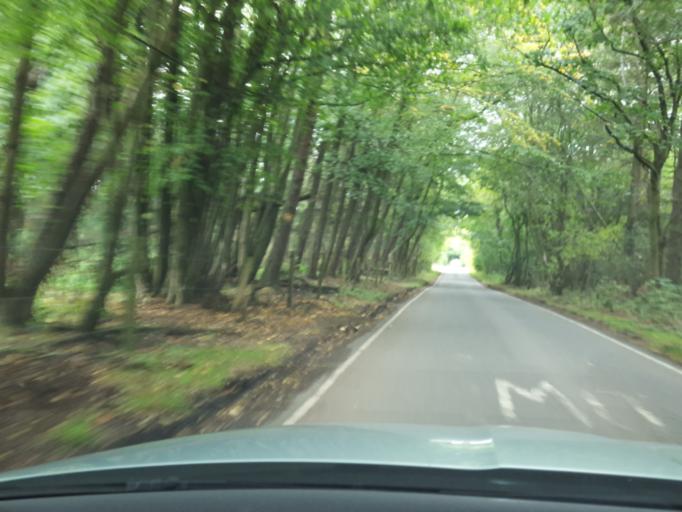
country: GB
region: Scotland
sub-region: West Lothian
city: Broxburn
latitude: 55.9149
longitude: -3.4582
